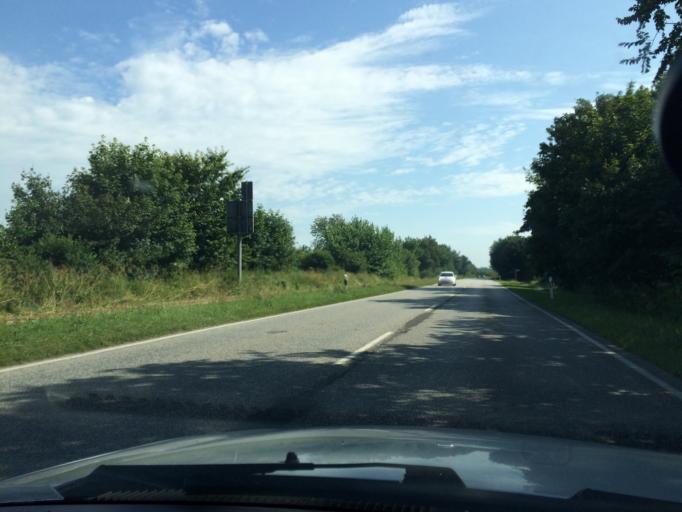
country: DE
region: Schleswig-Holstein
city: Jarplund-Weding
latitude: 54.7351
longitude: 9.4416
